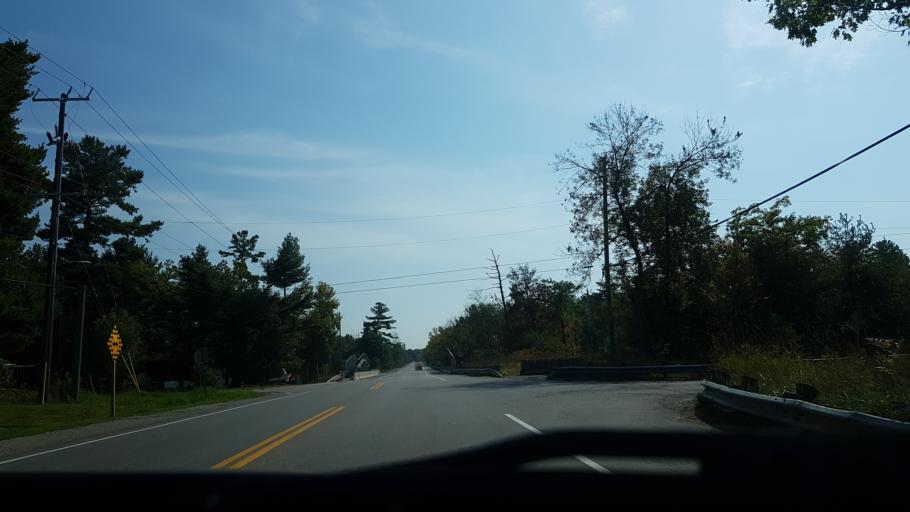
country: CA
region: Ontario
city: Orillia
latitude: 44.7470
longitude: -79.3263
